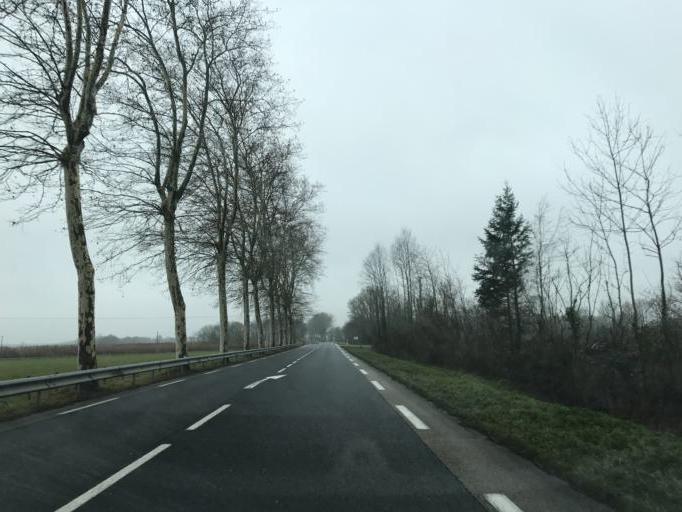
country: FR
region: Rhone-Alpes
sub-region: Departement de l'Ain
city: Saint-Paul-de-Varax
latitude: 46.0761
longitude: 5.0963
